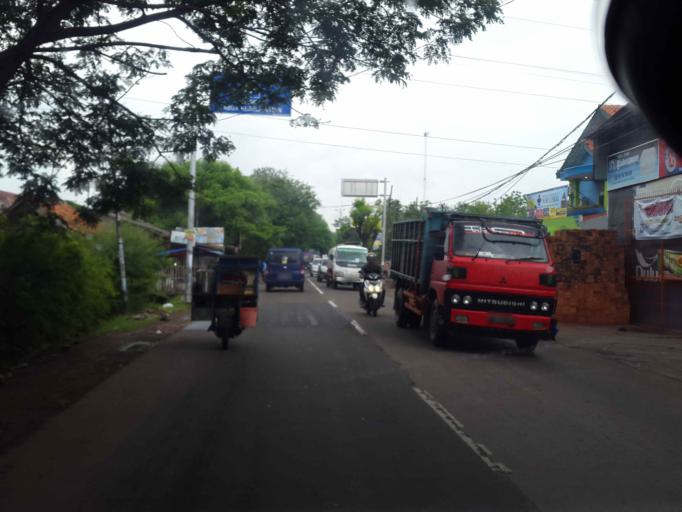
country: ID
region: West Java
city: Cikarang
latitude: -6.2532
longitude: 107.1574
